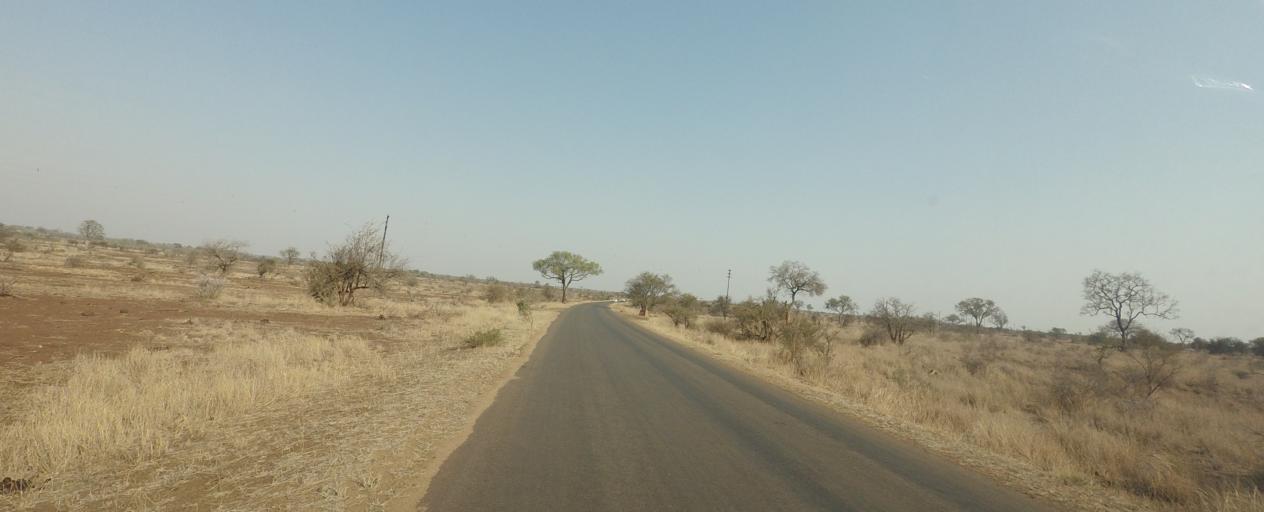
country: ZA
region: Limpopo
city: Thulamahashi
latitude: -24.3890
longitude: 31.7756
